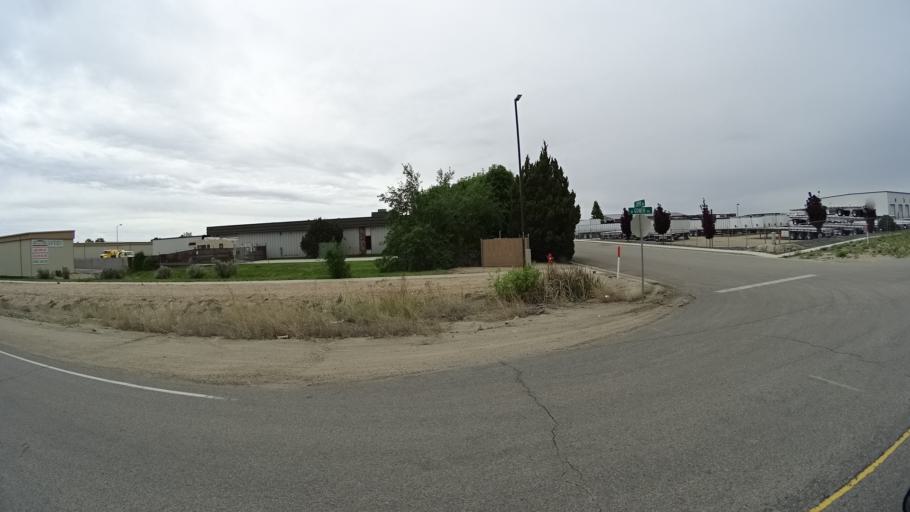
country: US
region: Idaho
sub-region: Ada County
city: Boise
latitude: 43.5456
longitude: -116.1817
